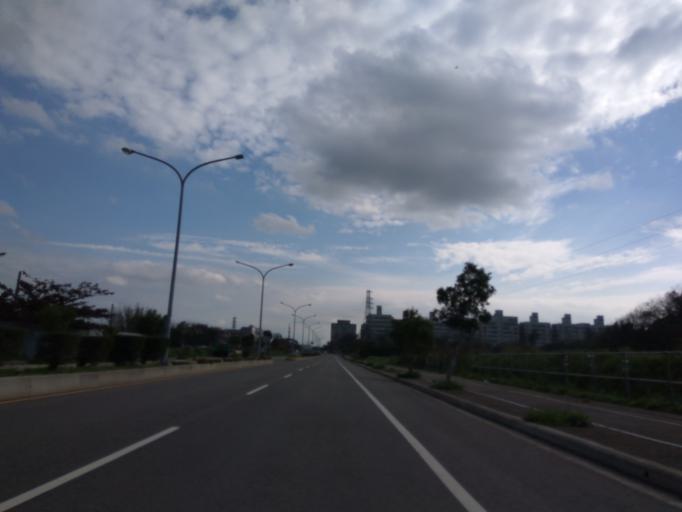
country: TW
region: Taiwan
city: Taoyuan City
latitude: 25.0673
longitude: 121.1746
